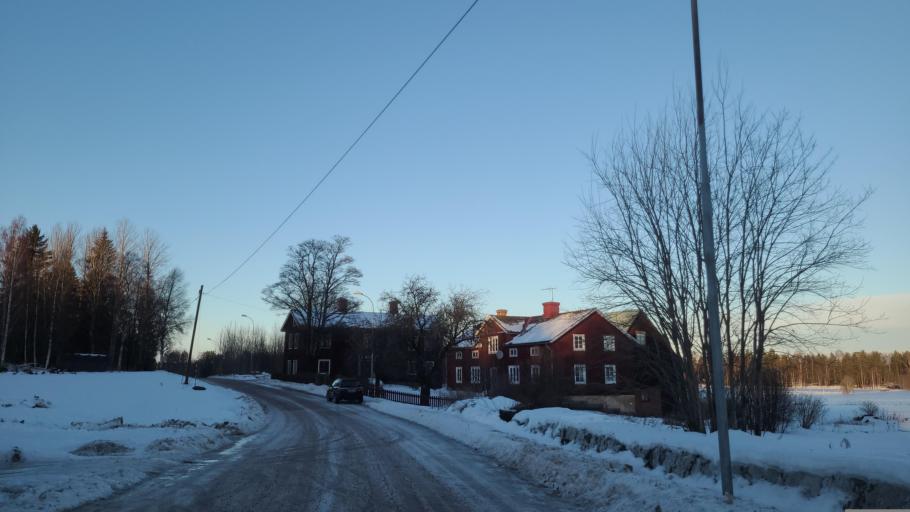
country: SE
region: Gaevleborg
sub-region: Soderhamns Kommun
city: Soderhamn
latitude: 61.2735
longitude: 16.9930
